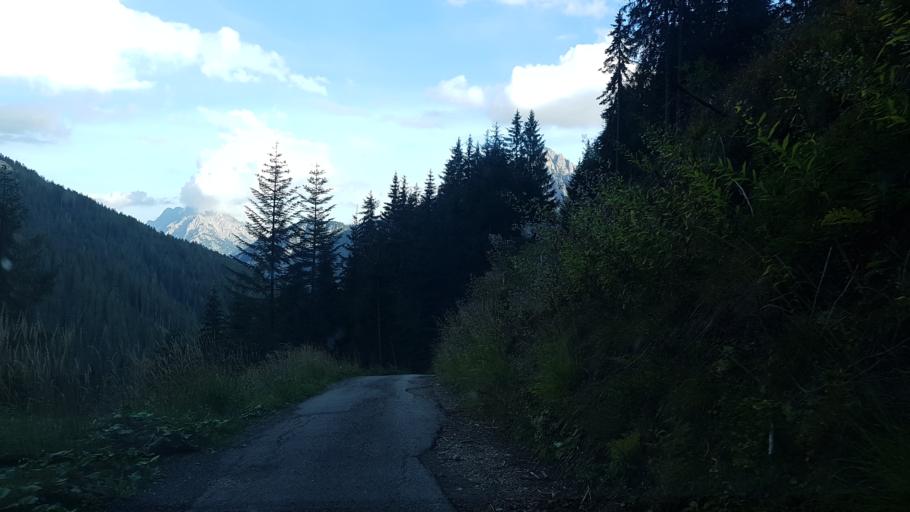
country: IT
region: Veneto
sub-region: Provincia di Belluno
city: San Pietro di Cadore
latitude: 46.5948
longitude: 12.5903
